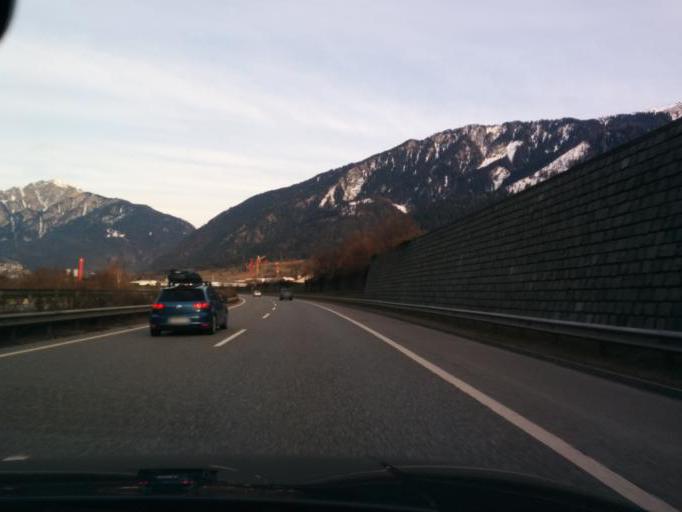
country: CH
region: Grisons
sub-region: Imboden District
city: Domat
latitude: 46.8372
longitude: 9.4547
